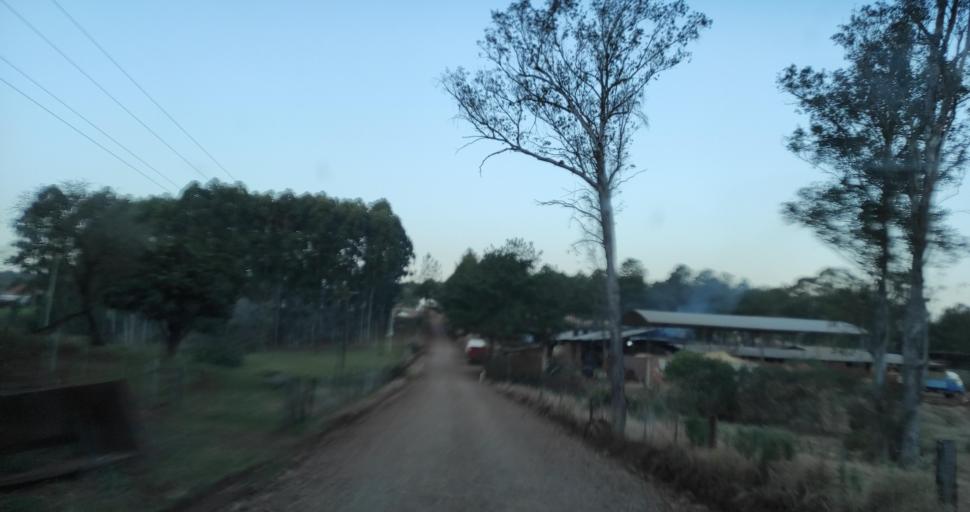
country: AR
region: Misiones
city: Capiovi
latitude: -26.8932
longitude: -55.0527
